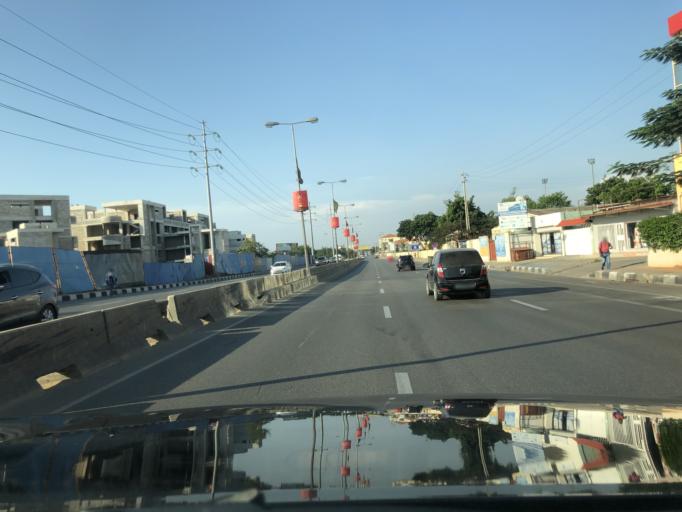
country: AO
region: Luanda
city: Luanda
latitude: -8.8983
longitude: 13.1776
